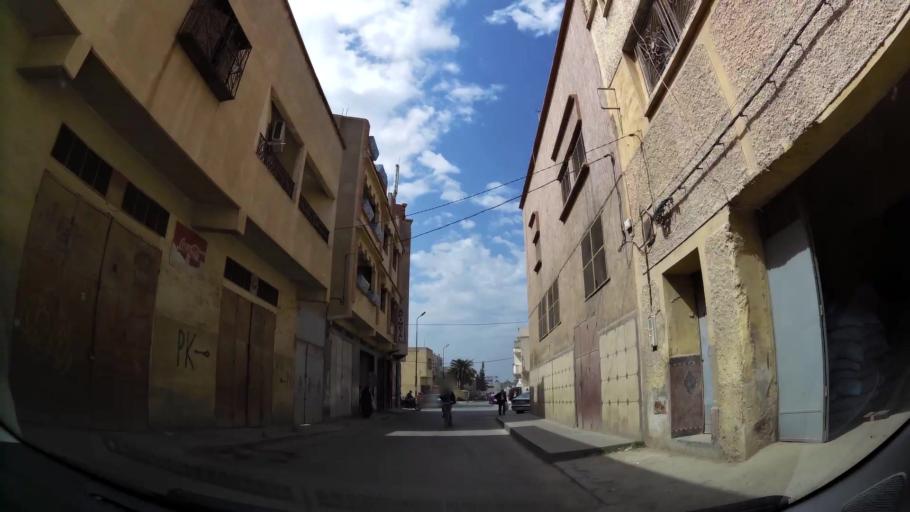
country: MA
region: Oriental
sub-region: Oujda-Angad
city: Oujda
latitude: 34.6820
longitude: -1.9062
